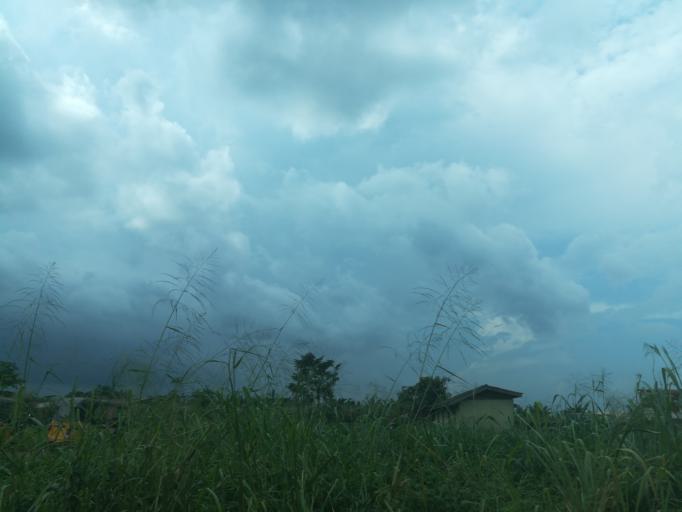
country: NG
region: Lagos
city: Ikorodu
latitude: 6.6445
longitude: 3.5566
